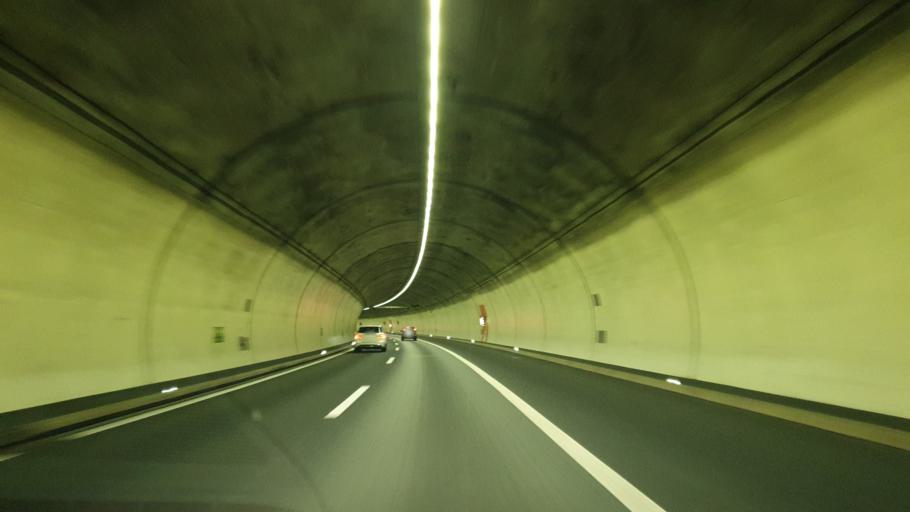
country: CH
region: Zurich
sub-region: Bezirk Dietikon
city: Birmensdorf
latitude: 47.3552
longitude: 8.4241
